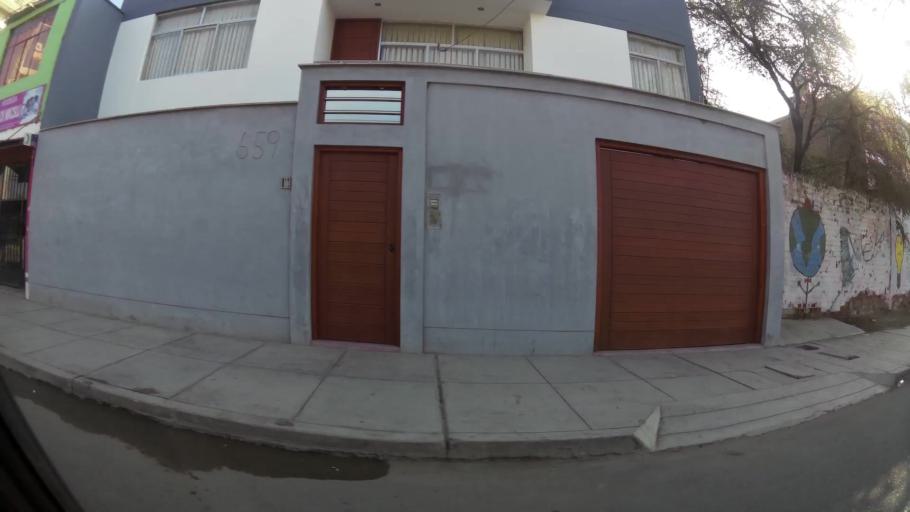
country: PE
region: Lambayeque
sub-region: Provincia de Chiclayo
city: Chiclayo
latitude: -6.7675
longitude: -79.8478
